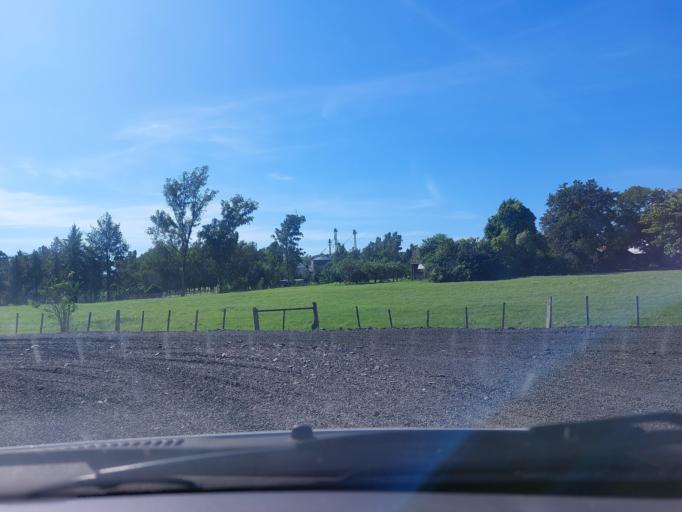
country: PY
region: San Pedro
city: Itacurubi del Rosario
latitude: -24.6101
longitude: -56.7944
